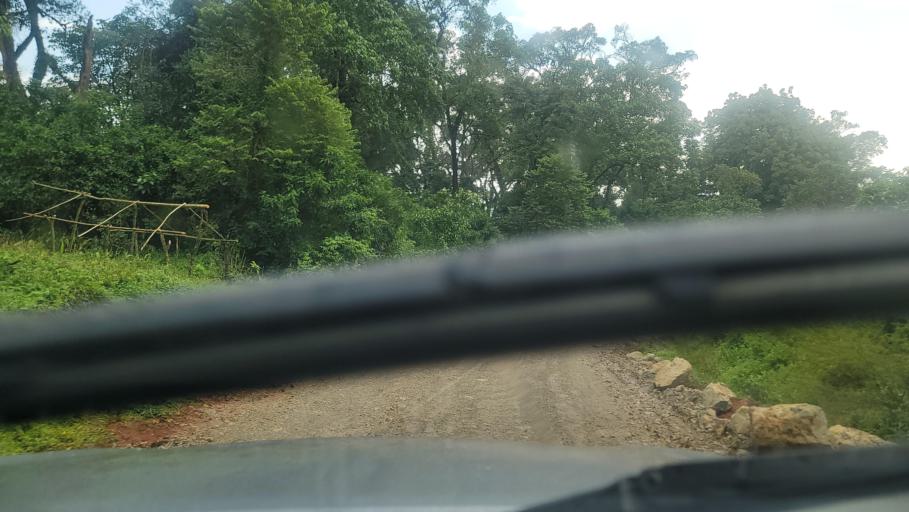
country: ET
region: Southern Nations, Nationalities, and People's Region
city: Bonga
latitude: 7.6490
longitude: 36.2469
